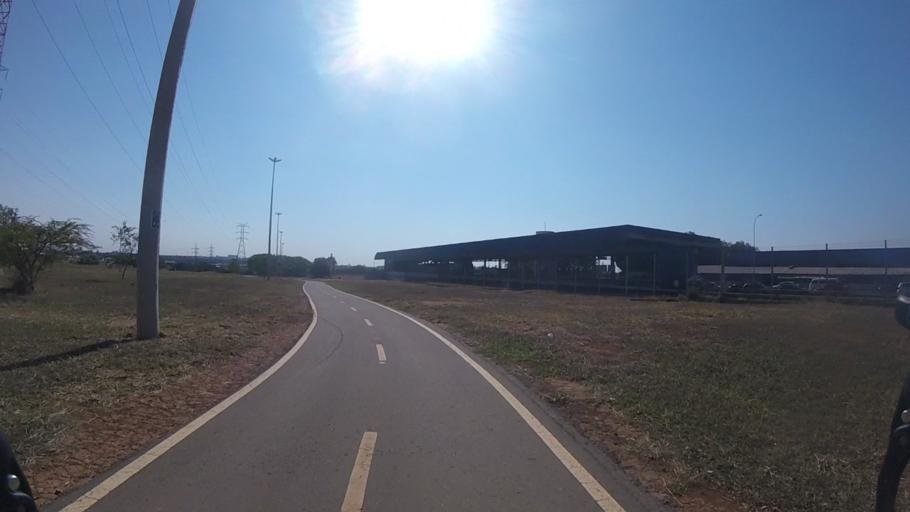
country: BR
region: Federal District
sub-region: Brasilia
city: Brasilia
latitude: -15.8230
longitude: -47.9760
